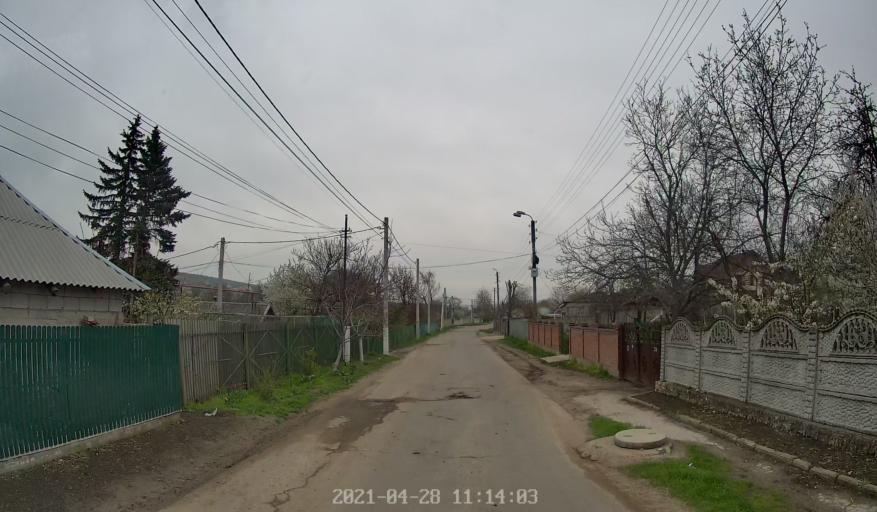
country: MD
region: Chisinau
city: Singera
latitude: 46.9819
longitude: 28.9371
